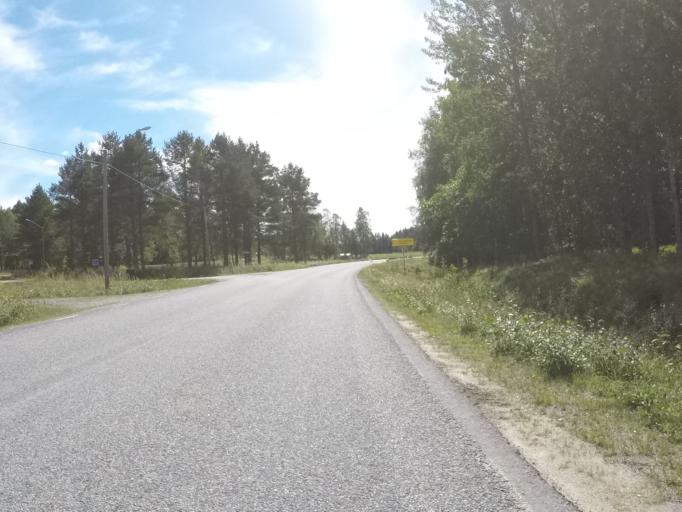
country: SE
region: Vaesterbotten
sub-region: Robertsfors Kommun
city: Robertsfors
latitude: 63.9674
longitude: 20.8123
